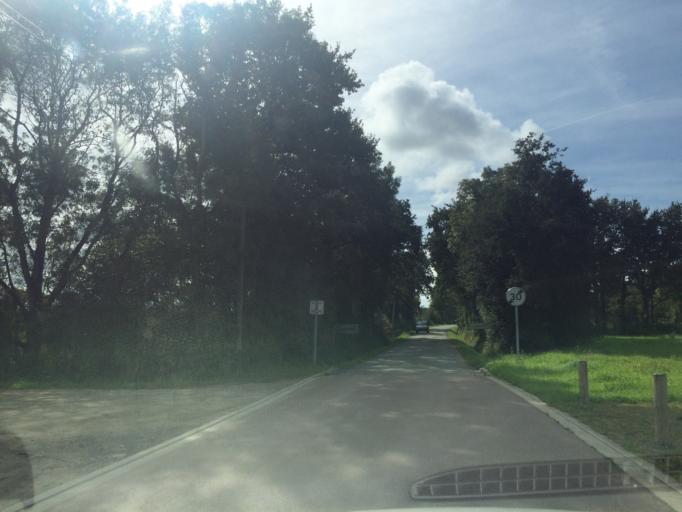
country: FR
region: Pays de la Loire
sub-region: Departement de la Loire-Atlantique
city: Chemere
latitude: 47.1127
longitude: -1.9171
